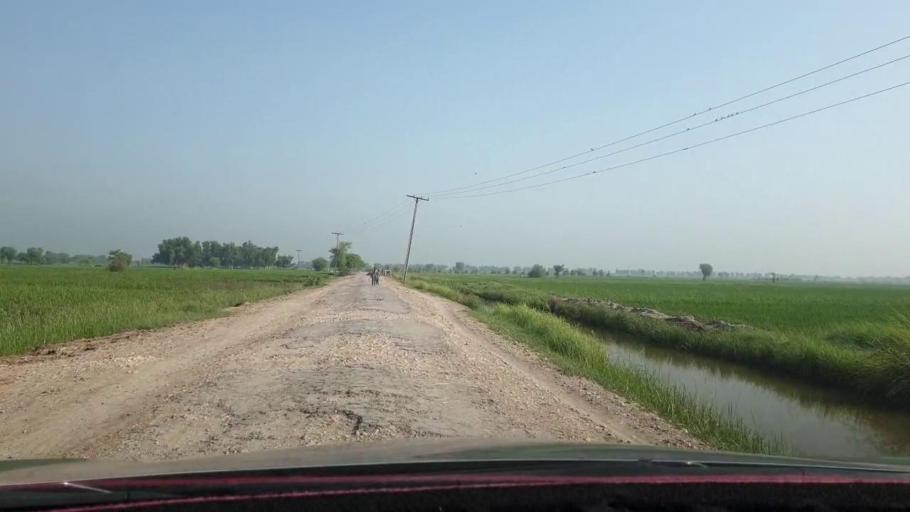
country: PK
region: Sindh
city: Nasirabad
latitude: 27.4382
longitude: 67.9206
